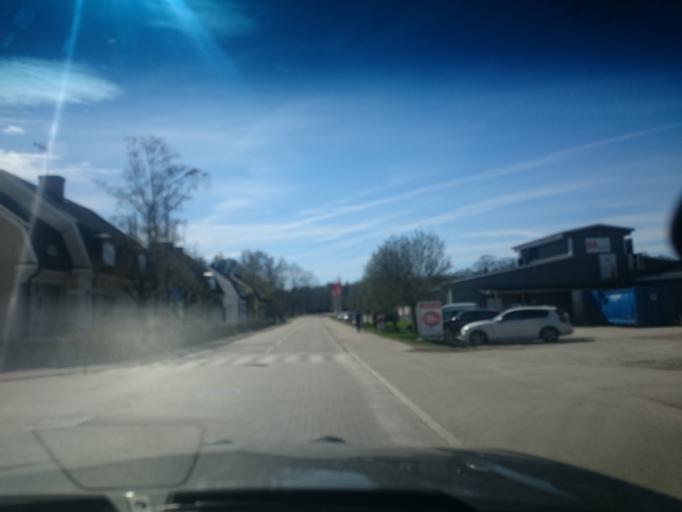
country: SE
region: Kalmar
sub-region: Hultsfreds Kommun
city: Virserum
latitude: 57.3206
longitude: 15.5778
